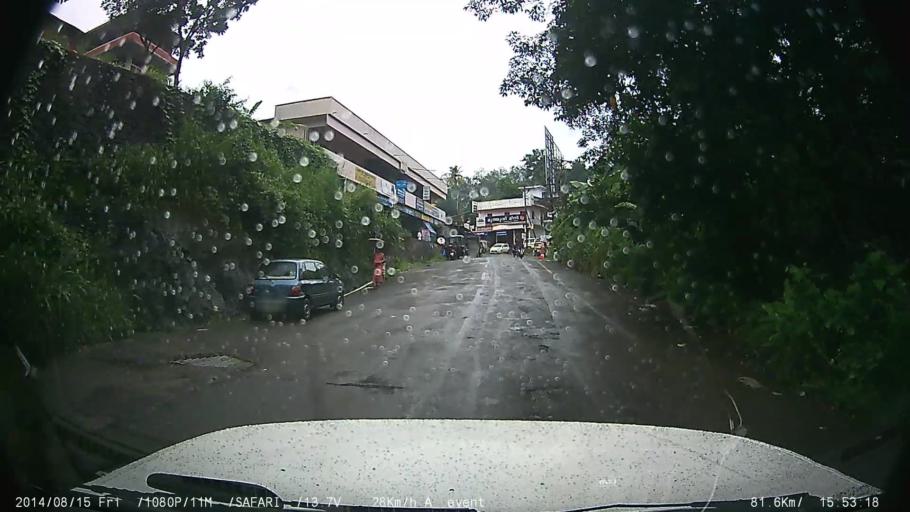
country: IN
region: Kerala
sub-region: Kottayam
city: Lalam
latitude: 9.8008
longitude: 76.7290
